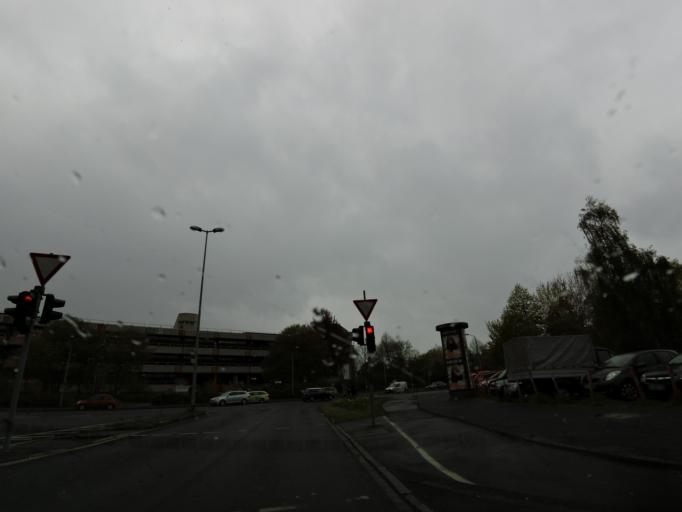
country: DE
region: Lower Saxony
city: Goettingen
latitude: 51.5402
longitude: 9.9247
